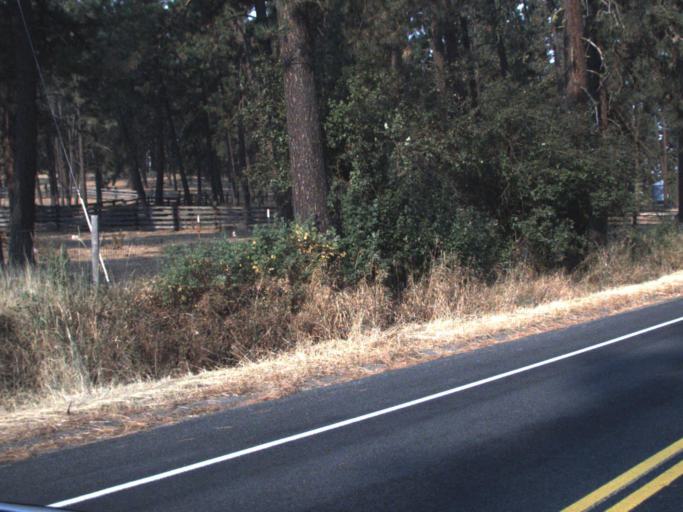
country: US
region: Idaho
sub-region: Benewah County
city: Plummer
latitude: 47.4402
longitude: -117.0605
